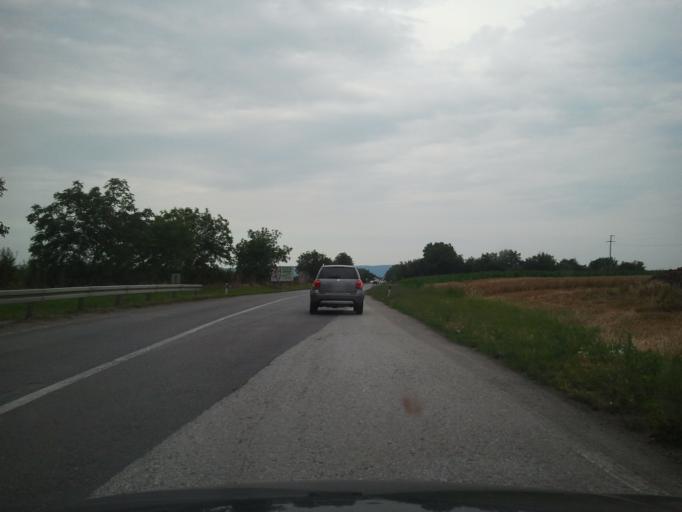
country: RS
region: Autonomna Pokrajina Vojvodina
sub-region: Sremski Okrug
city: Ruma
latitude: 45.0283
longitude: 19.8346
